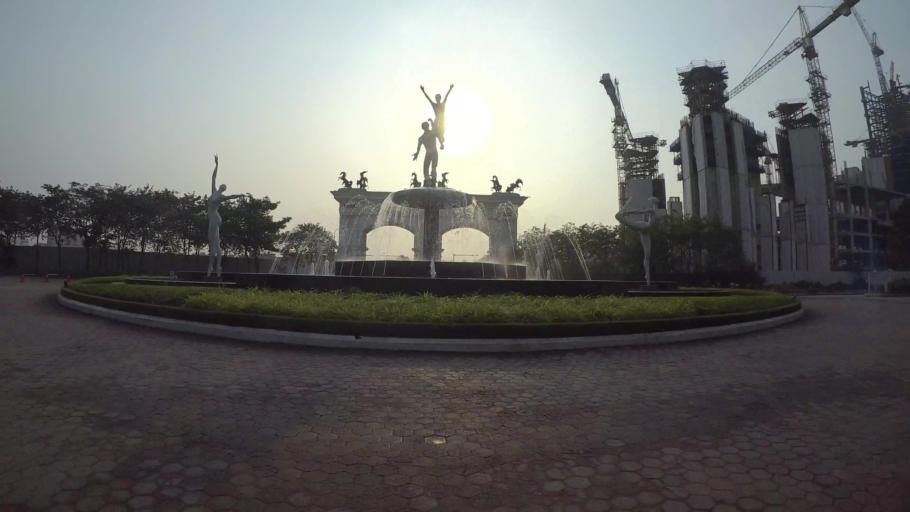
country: VN
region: Ha Noi
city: Tay Ho
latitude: 21.0809
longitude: 105.7910
